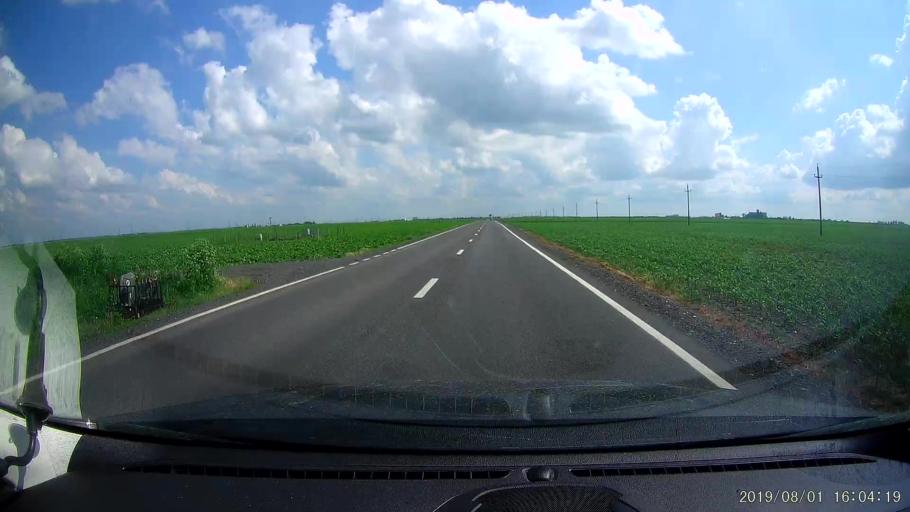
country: RO
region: Calarasi
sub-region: Comuna Dragalina
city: Drajna Noua
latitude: 44.4508
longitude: 27.3807
